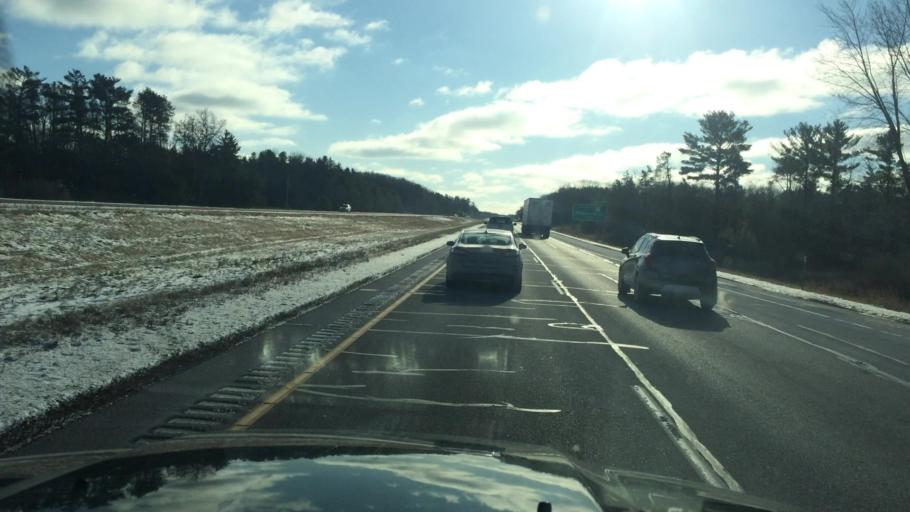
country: US
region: Wisconsin
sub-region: Portage County
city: Stevens Point
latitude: 44.5664
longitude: -89.5955
